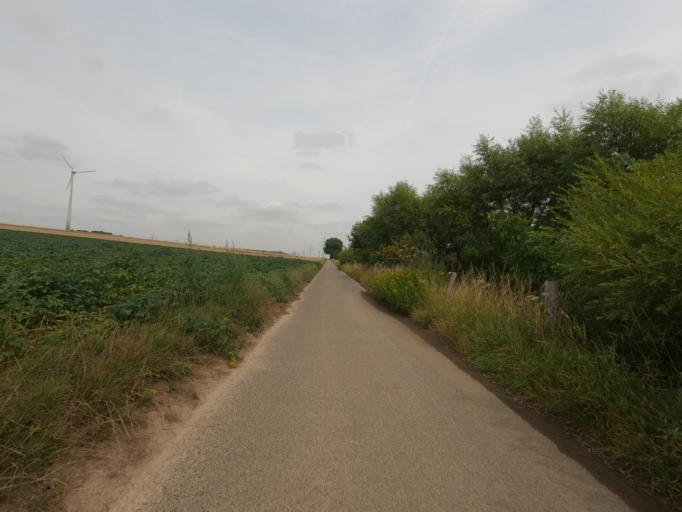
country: DE
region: North Rhine-Westphalia
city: Baesweiler
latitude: 50.9010
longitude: 6.2042
